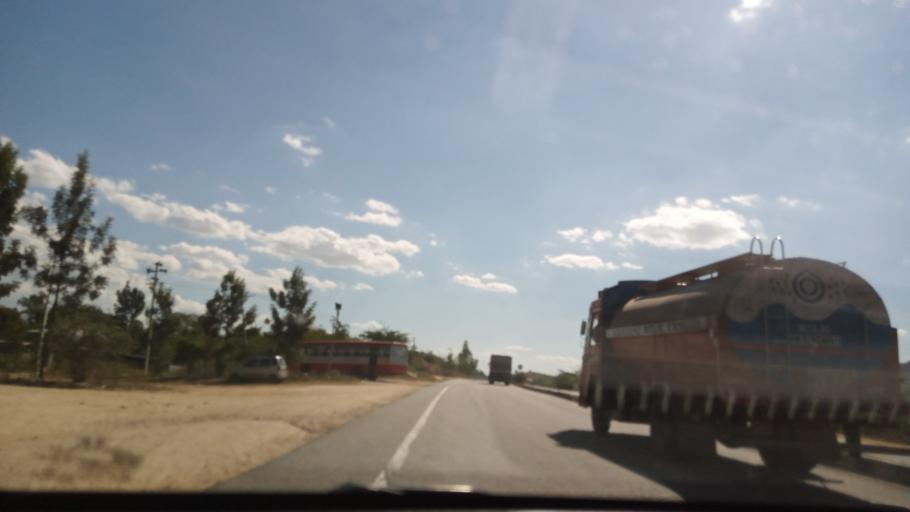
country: IN
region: Karnataka
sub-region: Kolar
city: Mulbagal
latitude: 13.1793
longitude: 78.4158
